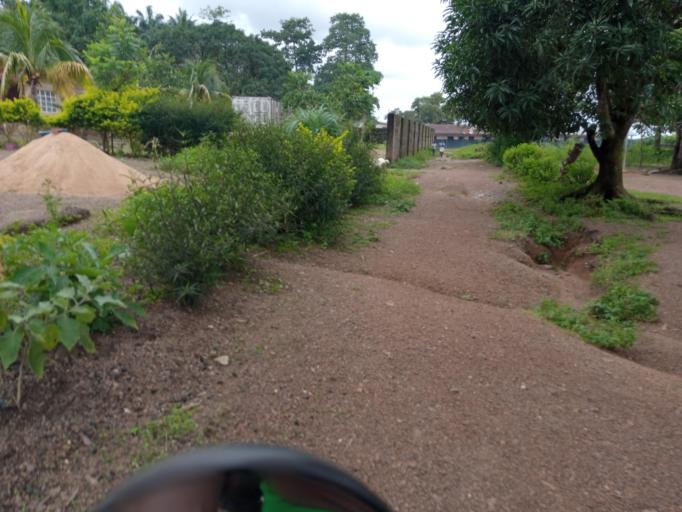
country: SL
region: Southern Province
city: Largo
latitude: 8.2037
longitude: -12.0573
